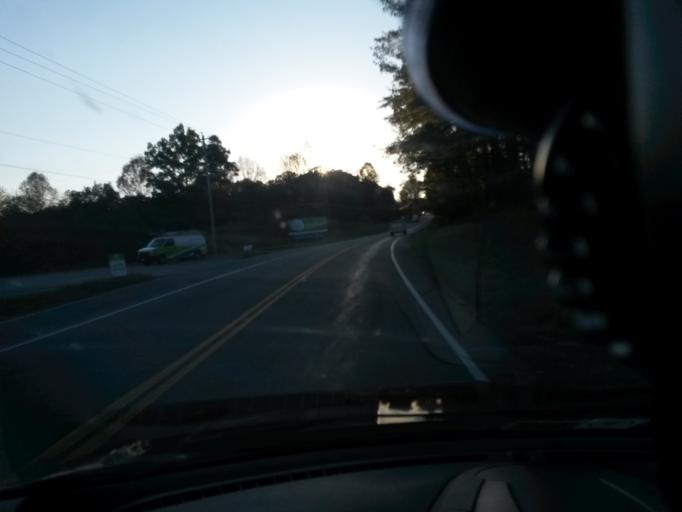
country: US
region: Virginia
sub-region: Franklin County
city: North Shore
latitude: 37.1273
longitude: -79.7506
